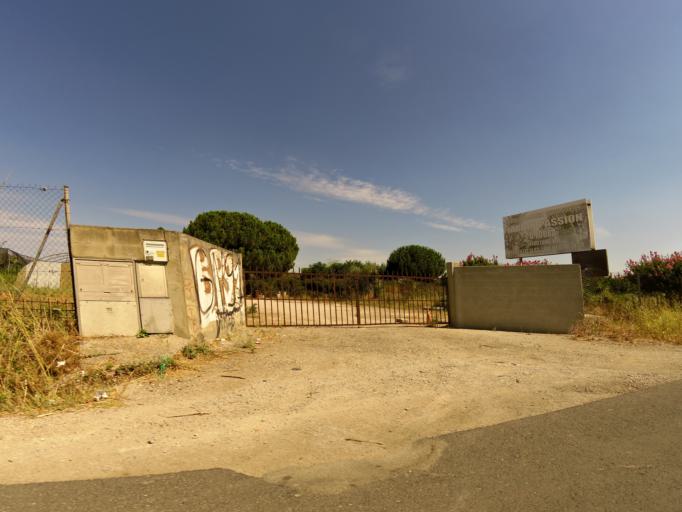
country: FR
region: Languedoc-Roussillon
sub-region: Departement de l'Herault
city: Lunel-Viel
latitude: 43.6760
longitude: 4.0803
